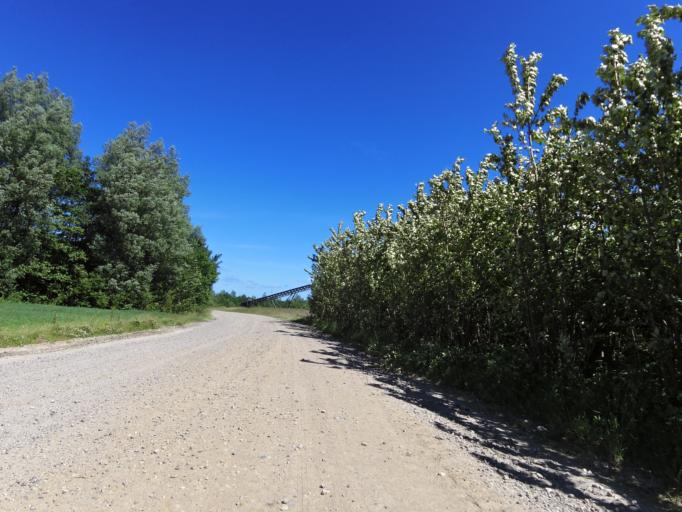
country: DK
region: South Denmark
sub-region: Aabenraa Kommune
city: Rodekro
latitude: 55.0602
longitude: 9.2989
